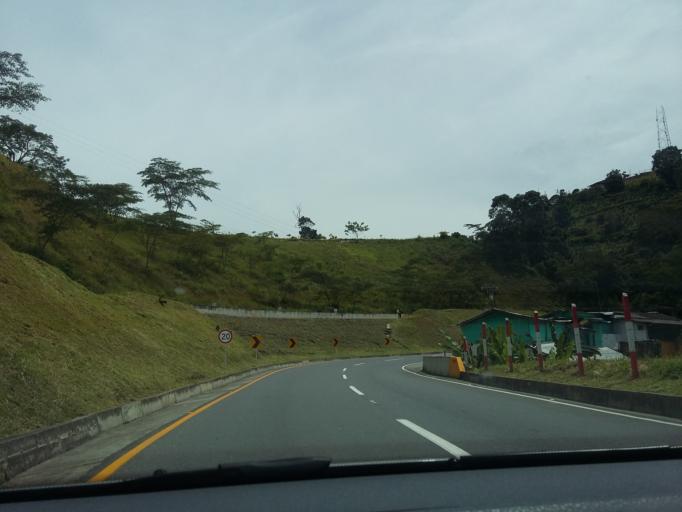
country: CO
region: Santander
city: Bucaramanga
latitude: 7.1173
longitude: -73.0792
